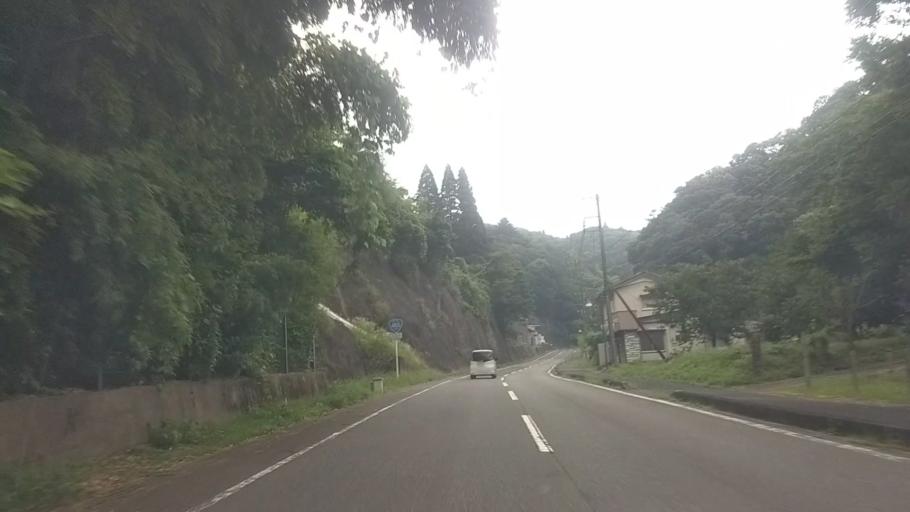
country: JP
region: Chiba
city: Kawaguchi
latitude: 35.2428
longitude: 140.1716
